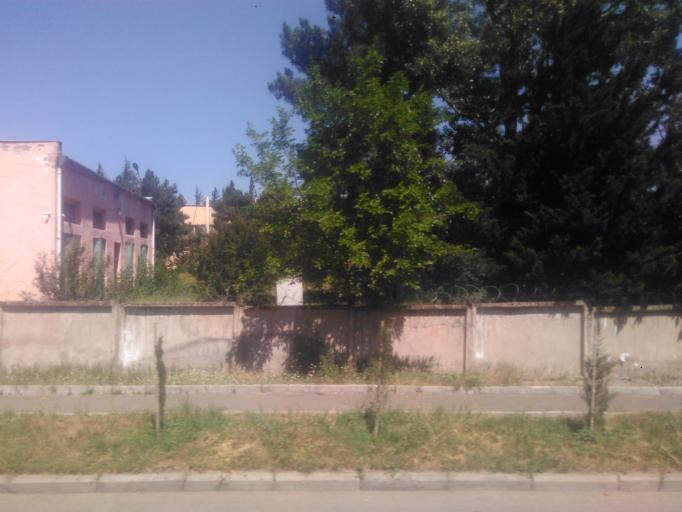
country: GE
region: T'bilisi
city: Tbilisi
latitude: 41.7039
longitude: 44.8878
